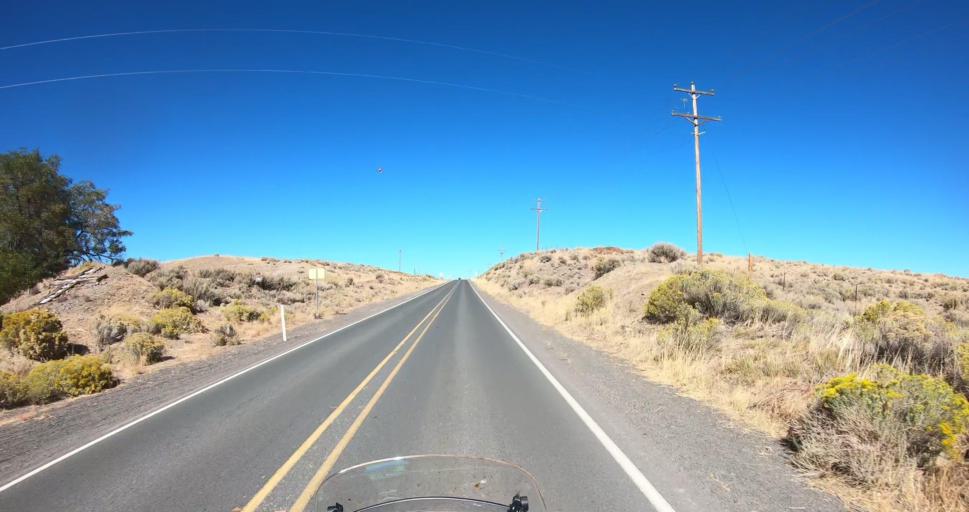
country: US
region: Oregon
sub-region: Lake County
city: Lakeview
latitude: 42.6971
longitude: -120.5462
